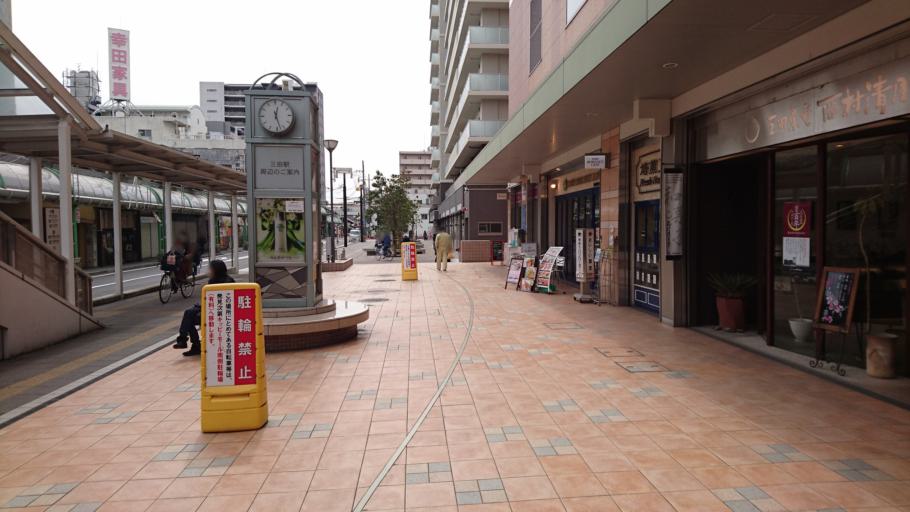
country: JP
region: Hyogo
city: Sandacho
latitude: 34.8880
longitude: 135.2295
